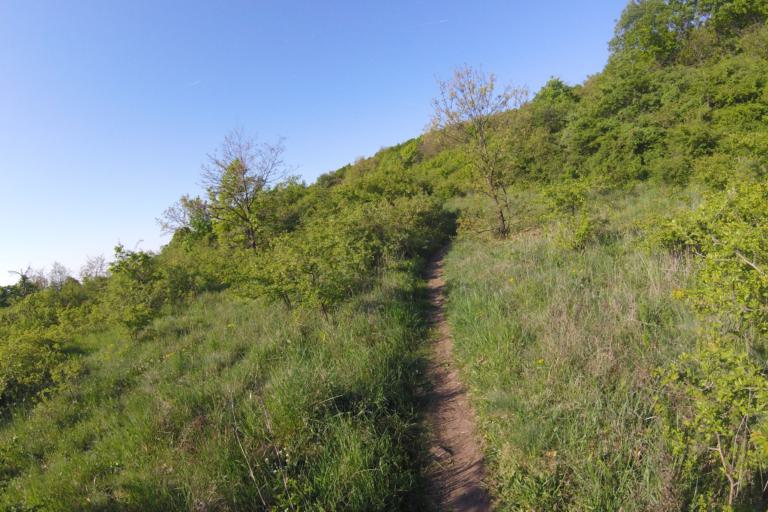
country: HU
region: Heves
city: Abasar
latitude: 47.8005
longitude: 19.9845
